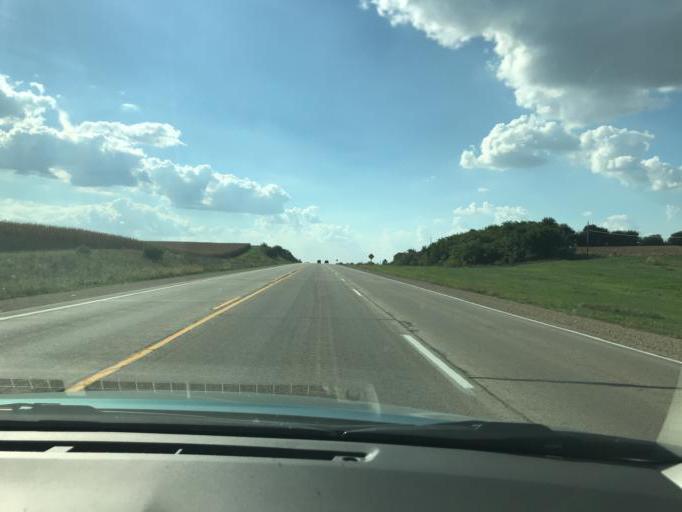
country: US
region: Wisconsin
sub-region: Green County
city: Brodhead
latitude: 42.5883
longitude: -89.4473
